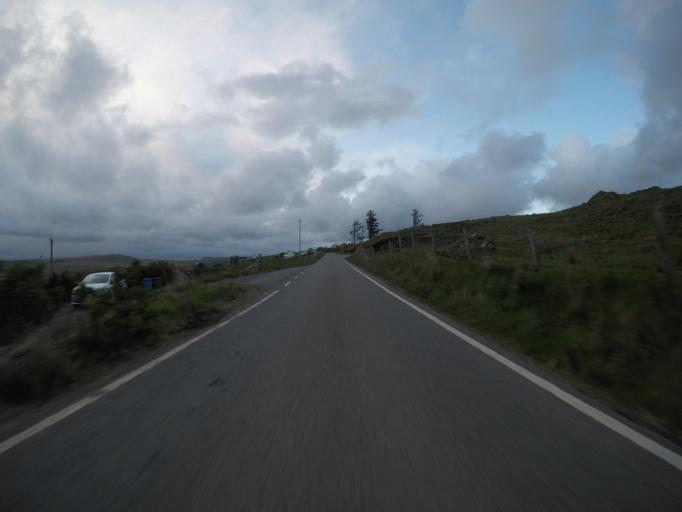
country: GB
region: Scotland
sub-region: Highland
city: Portree
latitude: 57.6251
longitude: -6.3774
